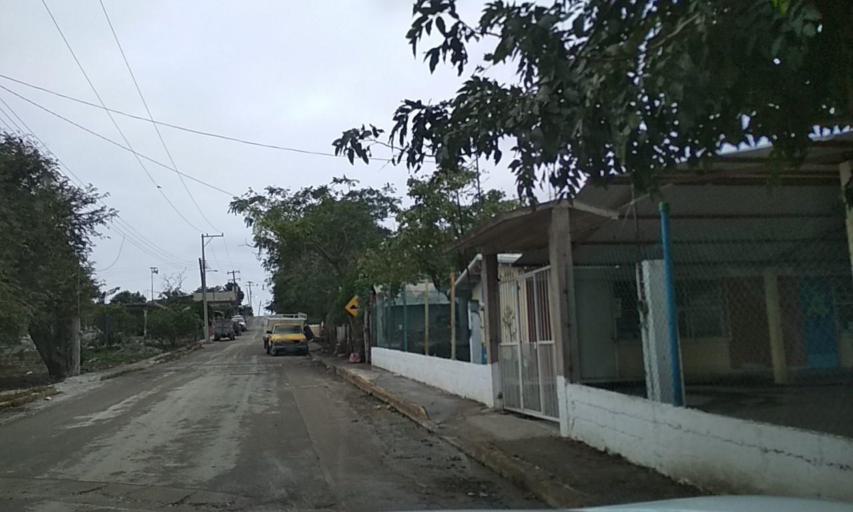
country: MX
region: Veracruz
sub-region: Papantla
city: El Chote
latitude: 20.3907
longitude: -97.3535
